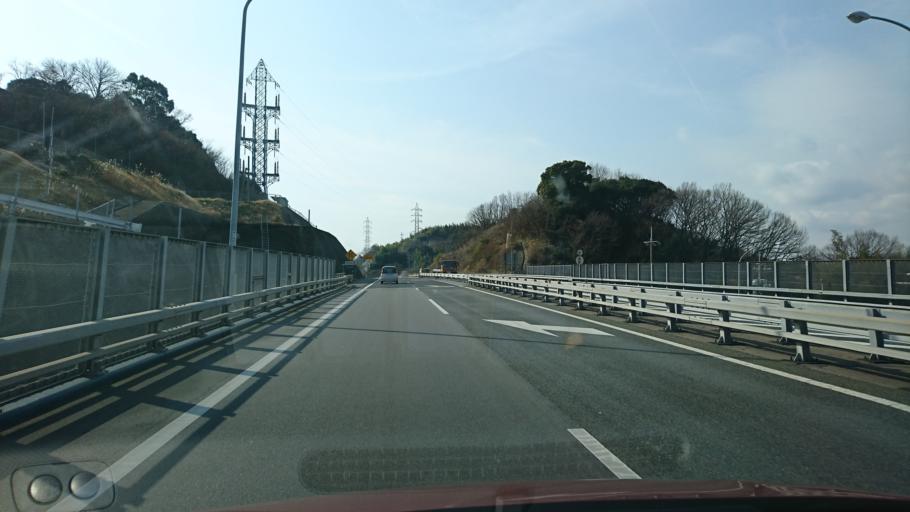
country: JP
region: Hiroshima
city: Onomichi
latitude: 34.4075
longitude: 133.2143
